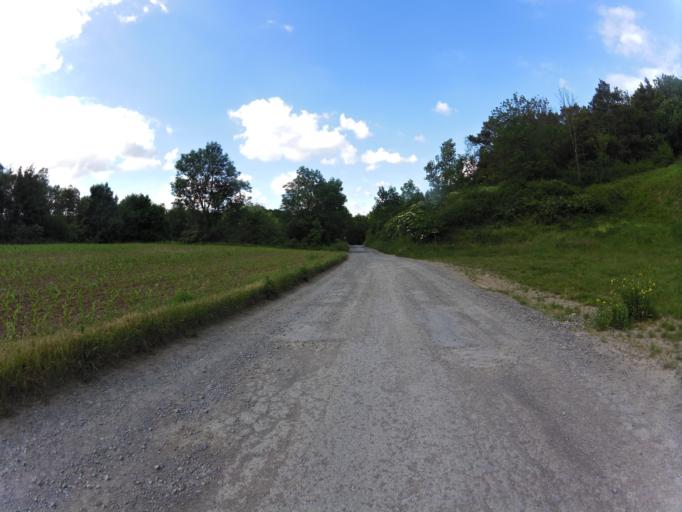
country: DE
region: Bavaria
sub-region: Regierungsbezirk Unterfranken
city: Sommerhausen
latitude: 49.6693
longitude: 10.0152
